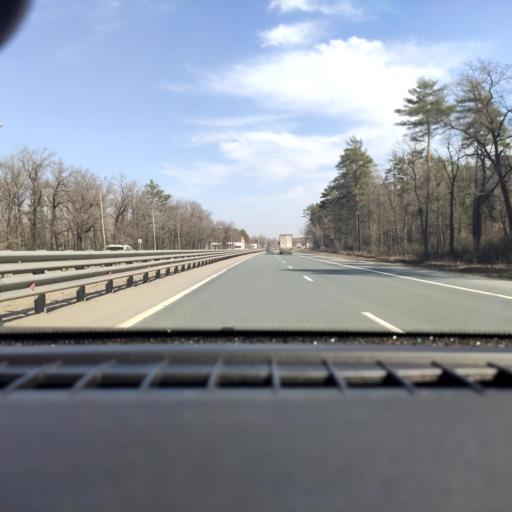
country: RU
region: Samara
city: Zhigulevsk
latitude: 53.5120
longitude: 49.5700
